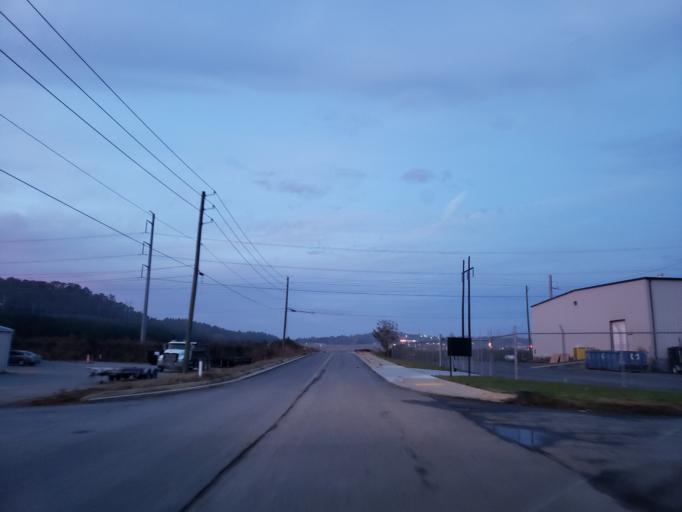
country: US
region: Georgia
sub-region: Bartow County
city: Cartersville
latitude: 34.2034
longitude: -84.8009
